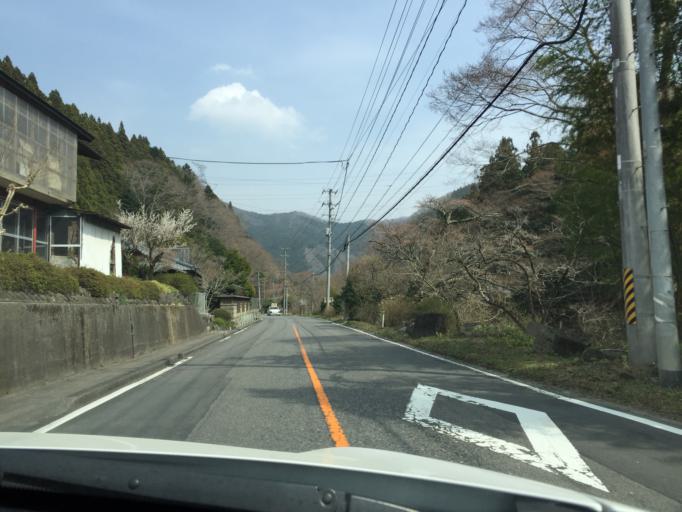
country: JP
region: Fukushima
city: Ishikawa
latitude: 37.0541
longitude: 140.6006
